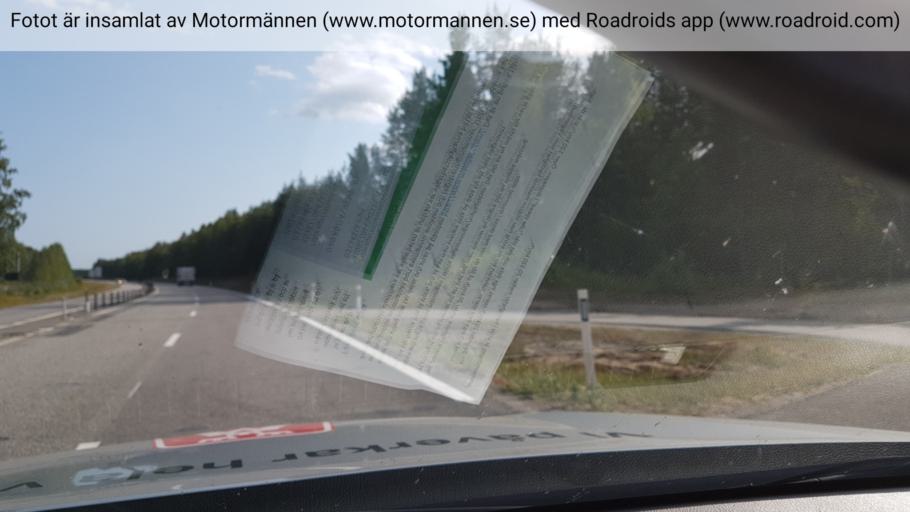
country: SE
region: Norrbotten
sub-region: Pitea Kommun
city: Bergsviken
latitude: 65.3069
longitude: 21.4084
